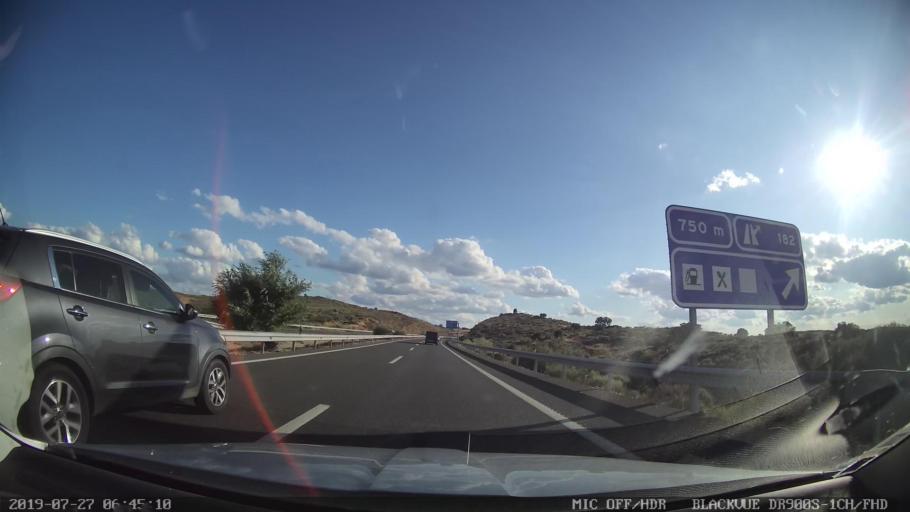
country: ES
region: Extremadura
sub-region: Provincia de Caceres
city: Navalmoral de la Mata
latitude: 39.8808
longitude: -5.5382
